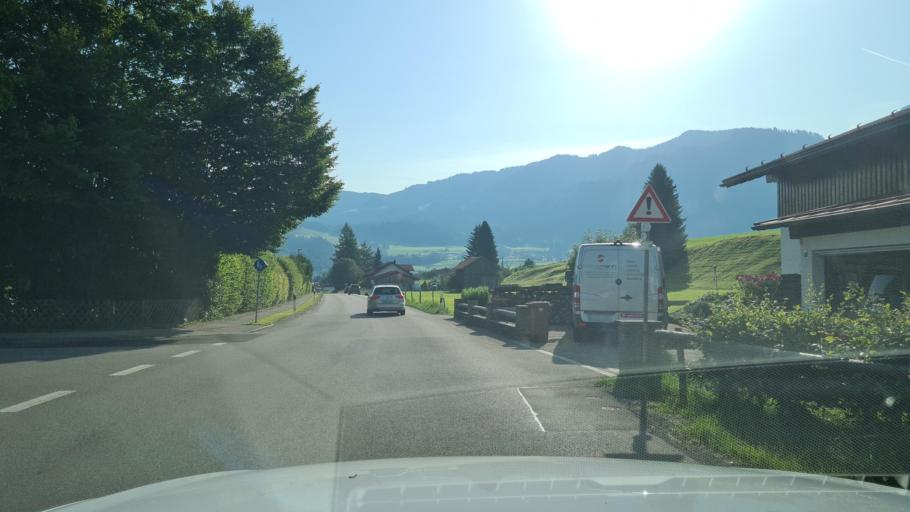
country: DE
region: Bavaria
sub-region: Swabia
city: Bolsterlang
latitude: 47.4588
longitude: 10.2601
